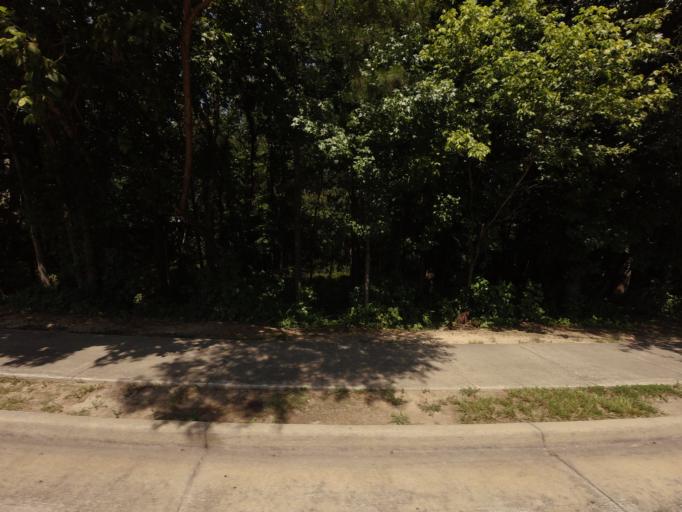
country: US
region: Georgia
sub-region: Fulton County
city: Johns Creek
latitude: 34.0111
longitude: -84.1832
